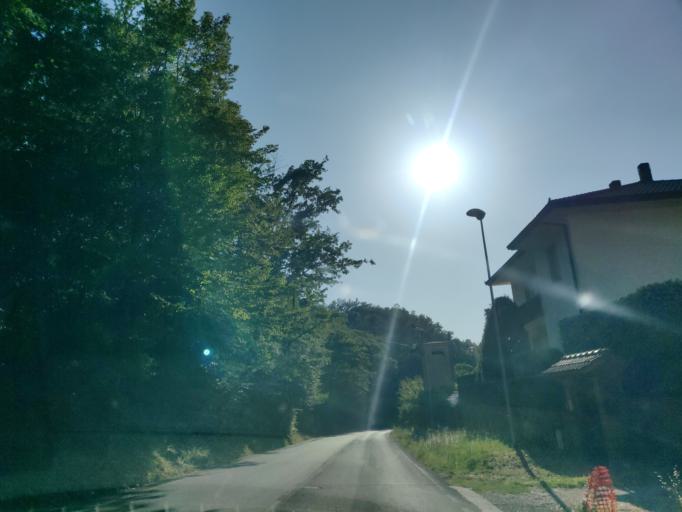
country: IT
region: Latium
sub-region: Citta metropolitana di Roma Capitale
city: Allumiere
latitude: 42.1529
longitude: 11.9065
